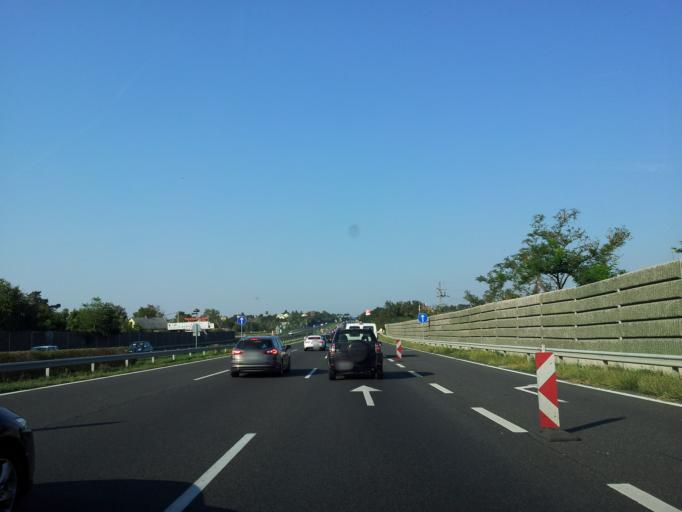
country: HU
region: Pest
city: Toeroekbalint
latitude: 47.4125
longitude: 18.8794
